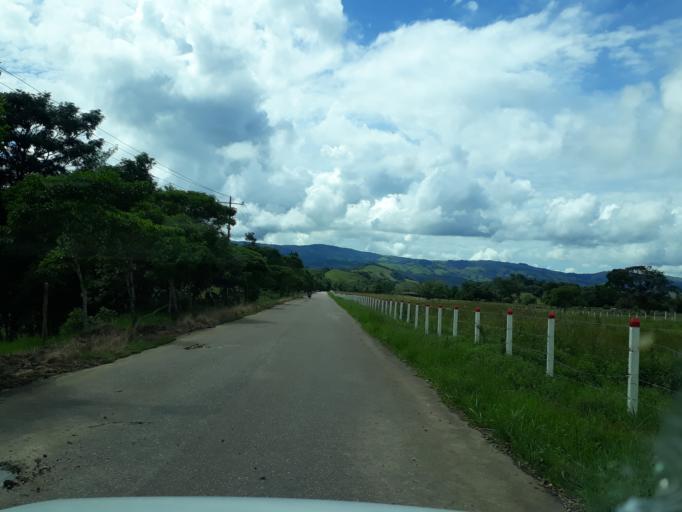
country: CO
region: Cundinamarca
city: Medina
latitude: 4.6433
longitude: -73.3198
